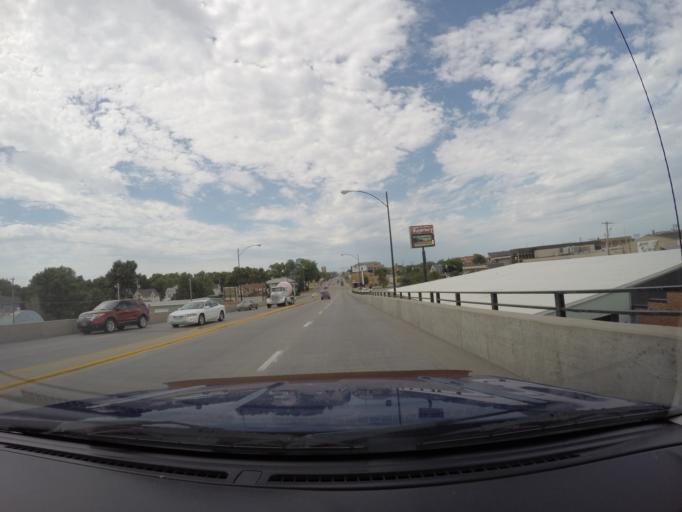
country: US
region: Nebraska
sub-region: Buffalo County
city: Kearney
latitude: 40.6953
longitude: -99.0844
